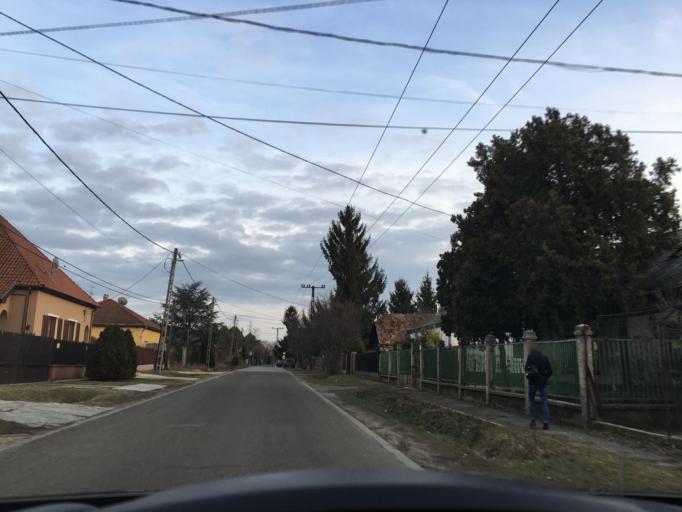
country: HU
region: Budapest
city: Budapest XVII. keruelet
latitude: 47.4822
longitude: 19.2817
